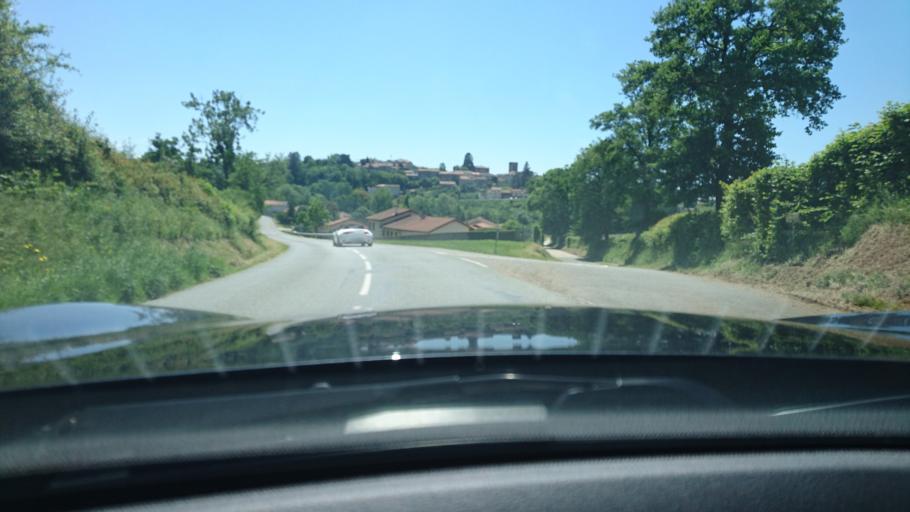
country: FR
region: Rhone-Alpes
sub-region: Departement de la Loire
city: Panissieres
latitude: 45.7997
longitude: 4.3401
